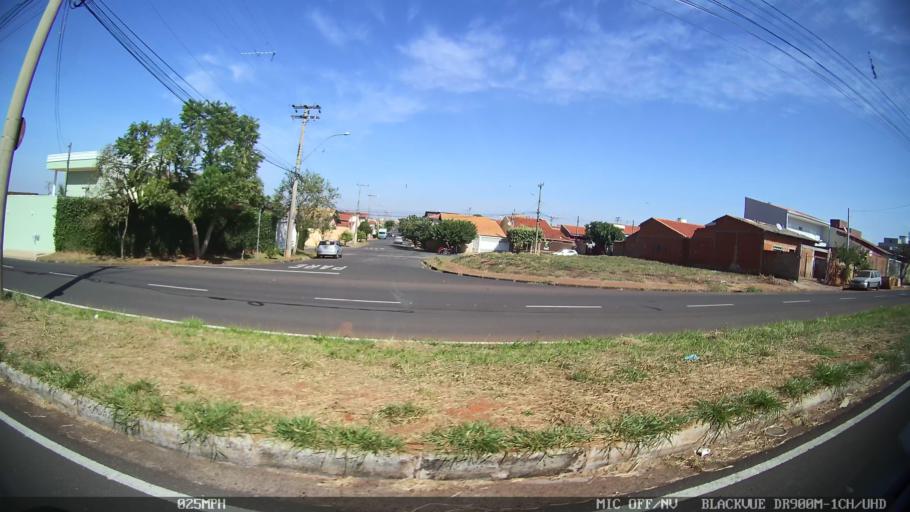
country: BR
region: Sao Paulo
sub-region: Sao Jose Do Rio Preto
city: Sao Jose do Rio Preto
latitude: -20.7813
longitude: -49.4177
